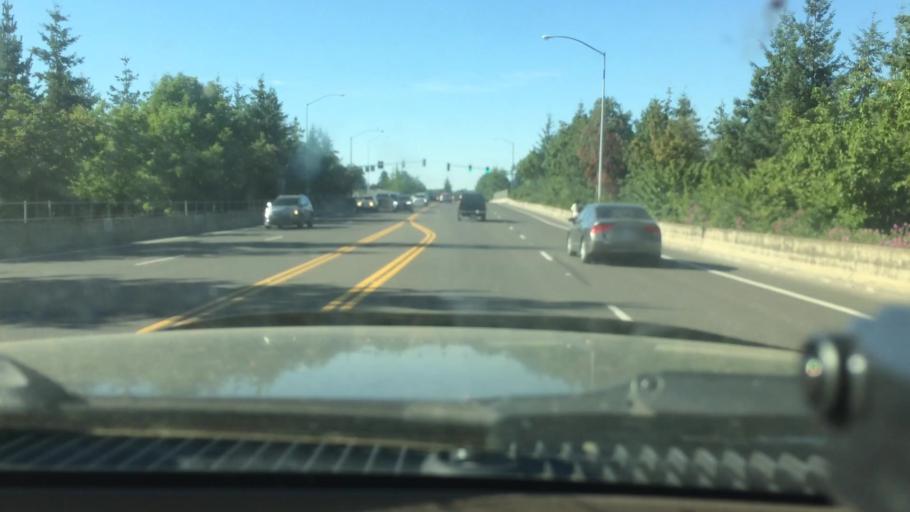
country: US
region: Oregon
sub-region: Lane County
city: Eugene
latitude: 44.0606
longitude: -123.1173
